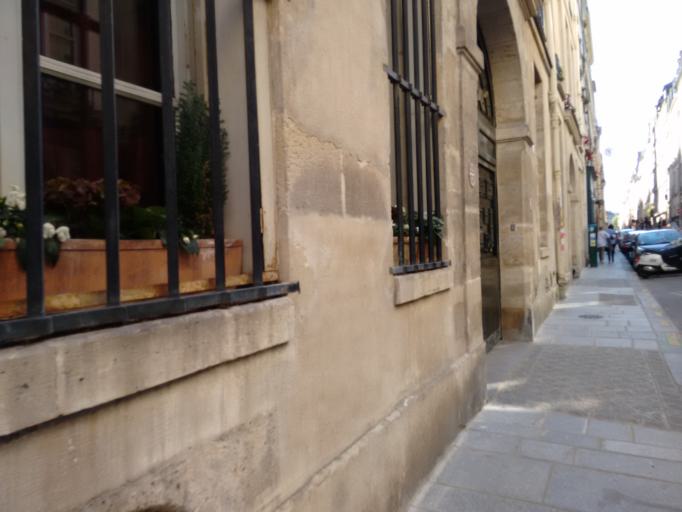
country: FR
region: Ile-de-France
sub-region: Paris
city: Paris
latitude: 48.8511
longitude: 2.3587
